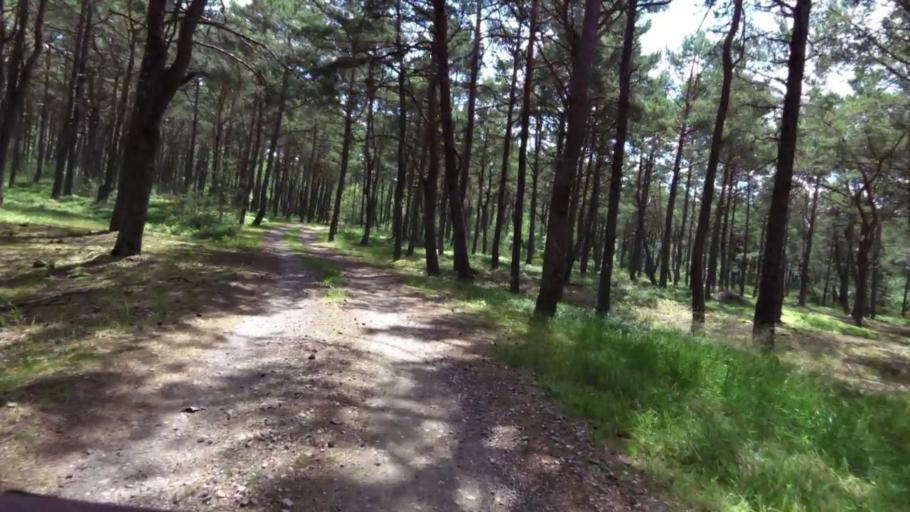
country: PL
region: West Pomeranian Voivodeship
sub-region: Powiat gryficki
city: Mrzezyno
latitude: 54.1212
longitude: 15.2272
